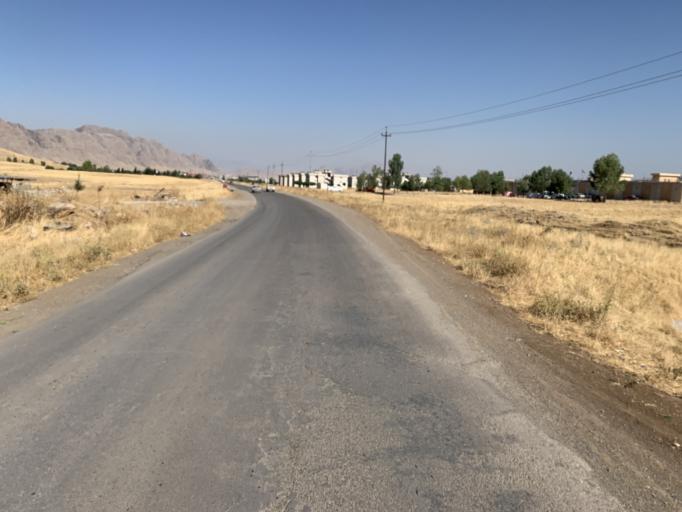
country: IQ
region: As Sulaymaniyah
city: Raniye
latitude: 36.2660
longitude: 44.8407
